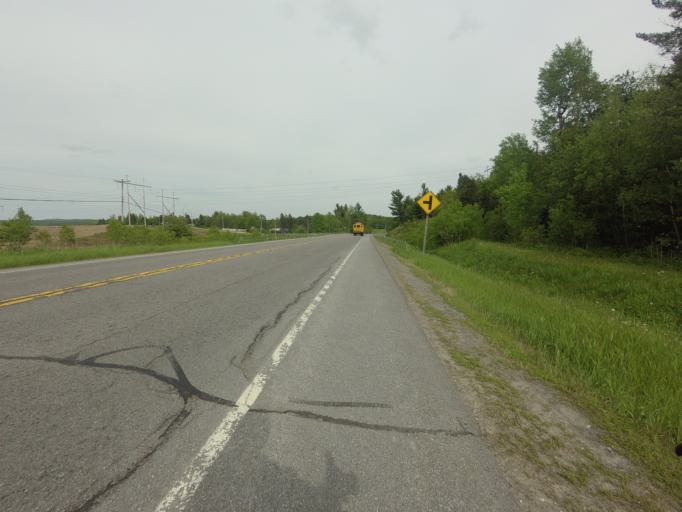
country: US
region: New York
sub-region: St. Lawrence County
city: Gouverneur
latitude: 44.3155
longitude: -75.2369
